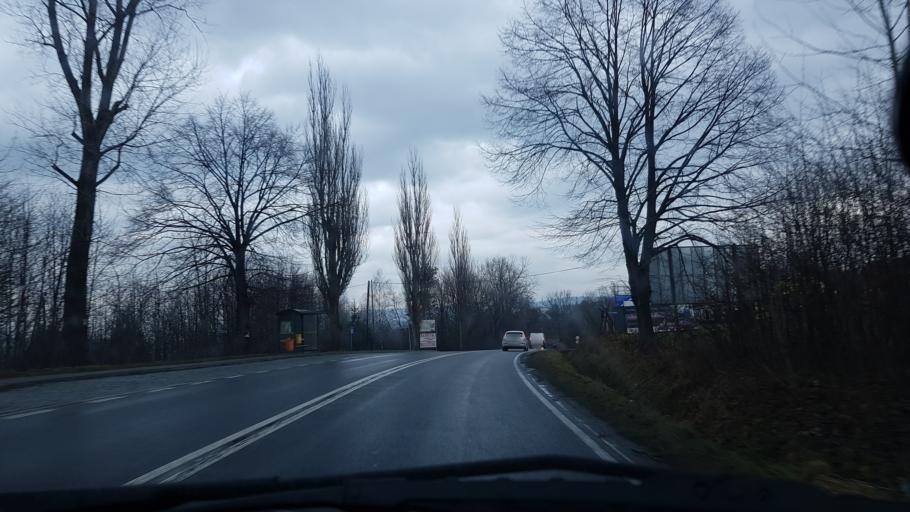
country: PL
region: Silesian Voivodeship
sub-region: Powiat zywiecki
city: Lekawica
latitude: 49.7109
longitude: 19.2260
